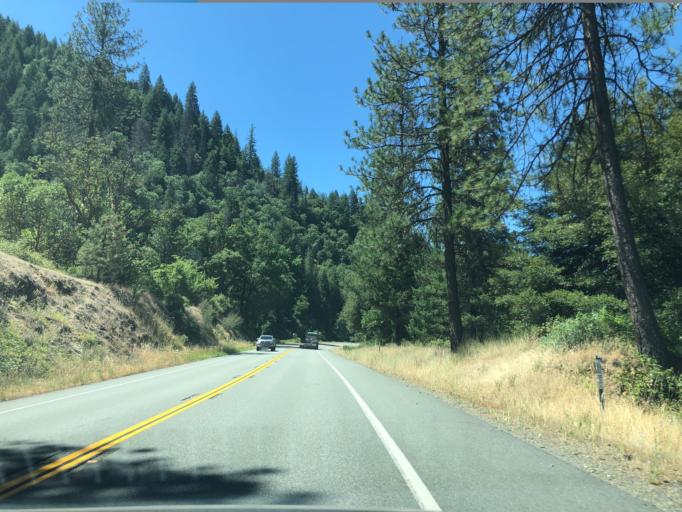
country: US
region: California
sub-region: Trinity County
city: Weaverville
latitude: 40.6847
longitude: -122.9345
